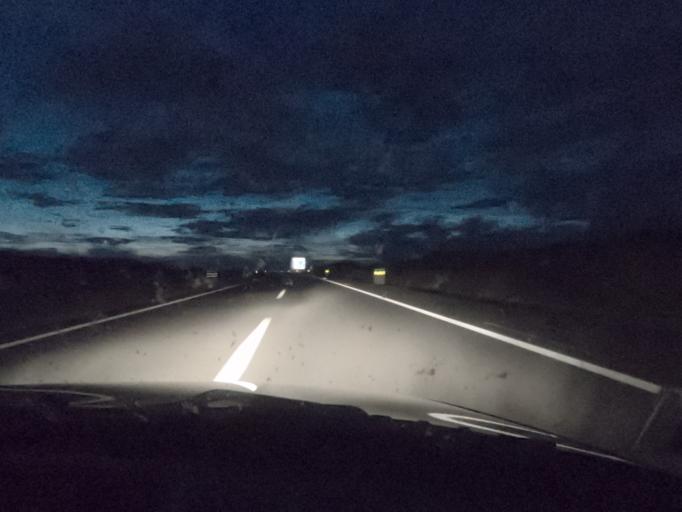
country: ES
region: Extremadura
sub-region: Provincia de Caceres
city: Morcillo
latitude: 39.9876
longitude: -6.4315
